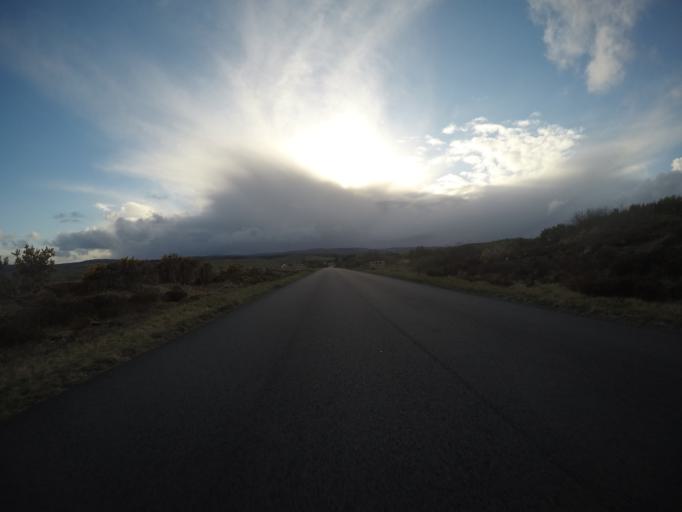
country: GB
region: Scotland
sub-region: Highland
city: Portree
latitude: 57.4506
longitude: -6.2731
